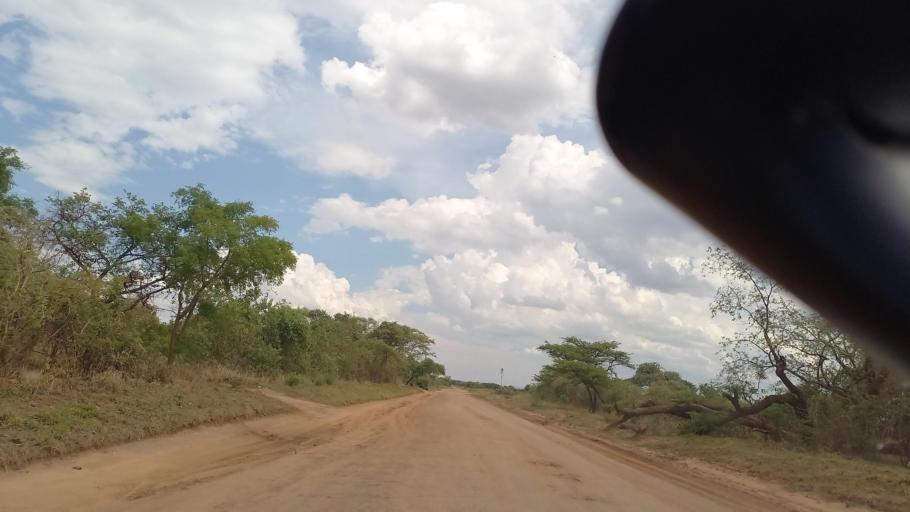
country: ZM
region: Southern
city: Nakambala
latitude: -16.0525
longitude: 27.9855
